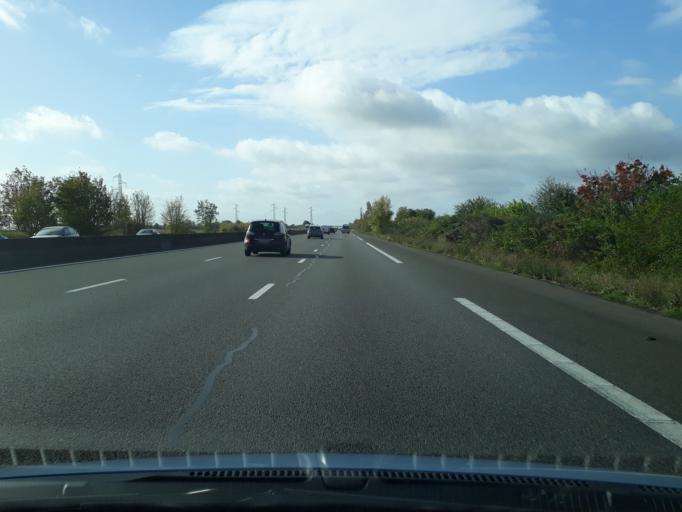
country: FR
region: Centre
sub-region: Departement du Loiret
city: Beaugency
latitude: 47.8004
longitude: 1.6141
